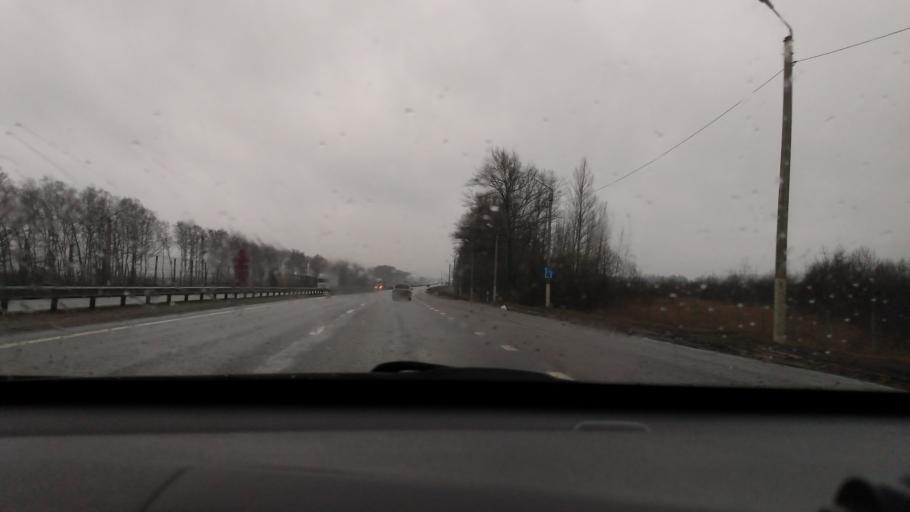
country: RU
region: Moskovskaya
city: Ozherel'ye
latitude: 54.5997
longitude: 38.1685
